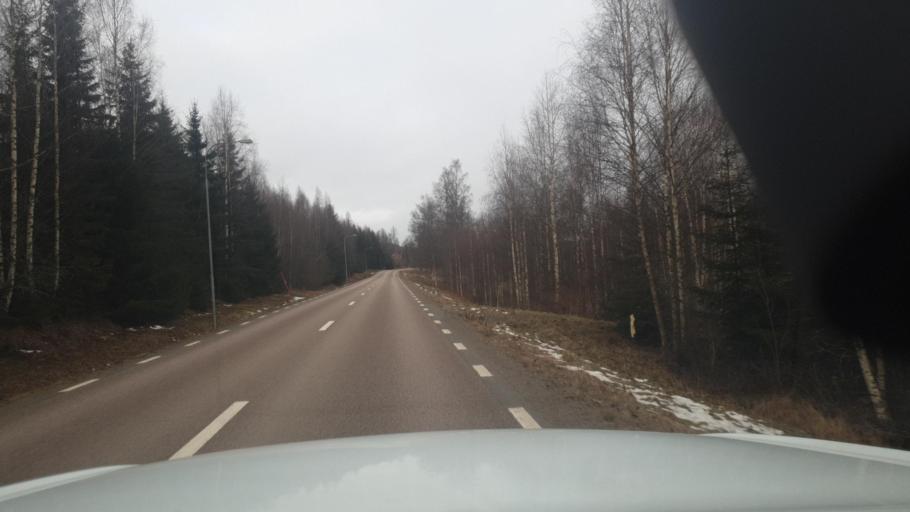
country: SE
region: Vaermland
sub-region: Sunne Kommun
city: Sunne
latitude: 59.8786
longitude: 12.9310
